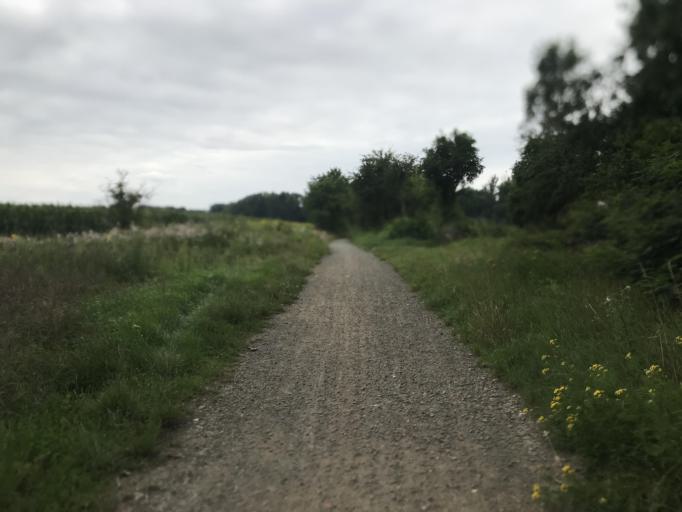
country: DE
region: Saxony-Anhalt
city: Quedlinburg
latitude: 51.7737
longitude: 11.1200
